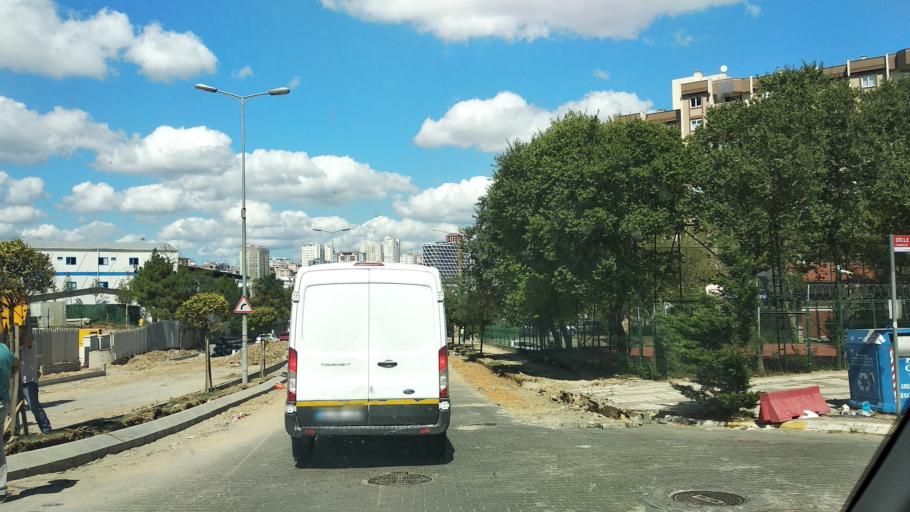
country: TR
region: Istanbul
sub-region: Atasehir
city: Atasehir
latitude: 40.9943
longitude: 29.1280
